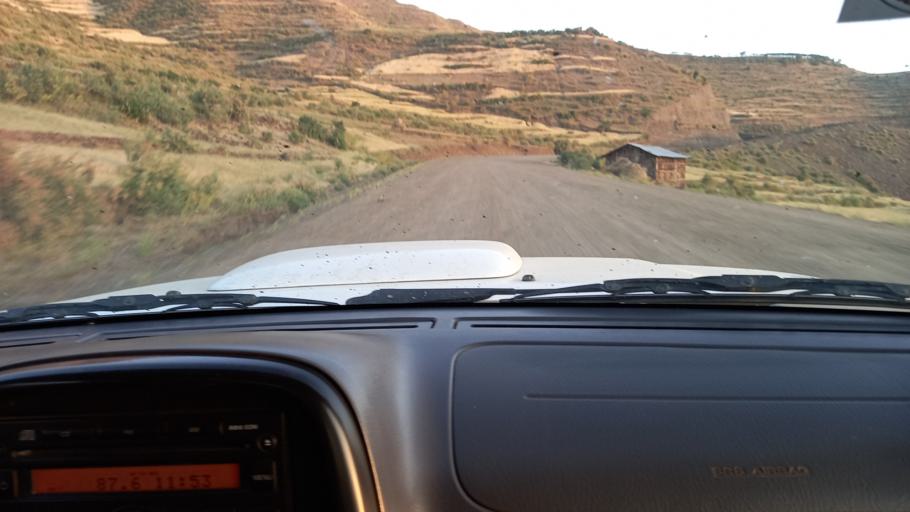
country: ET
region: Amhara
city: Debark'
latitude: 13.0532
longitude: 38.0190
